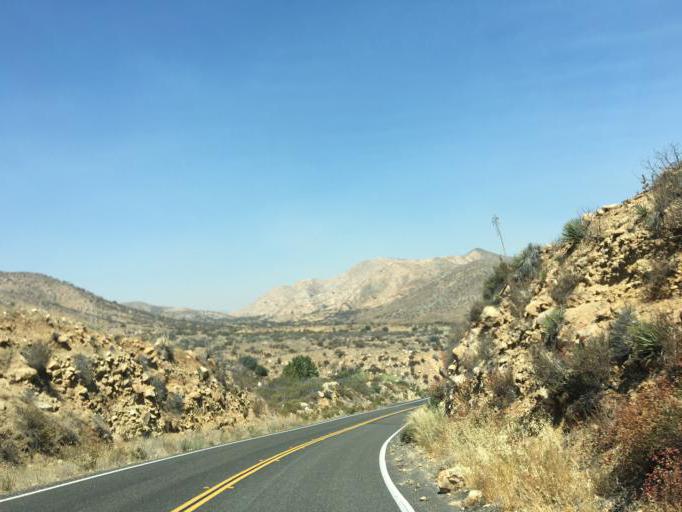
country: US
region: California
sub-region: Los Angeles County
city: Acton
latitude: 34.4424
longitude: -118.1488
